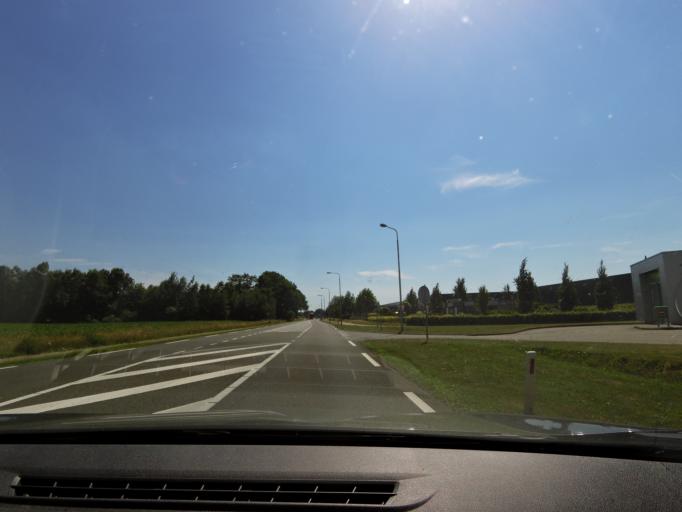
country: NL
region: Gelderland
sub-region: Berkelland
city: Eibergen
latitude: 52.0562
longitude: 6.6271
